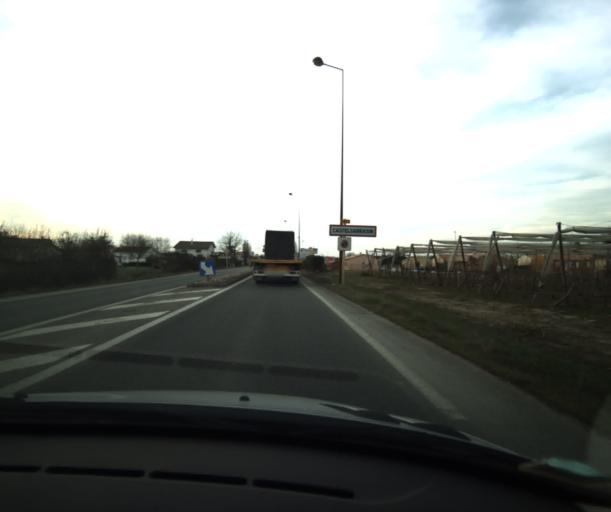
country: FR
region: Midi-Pyrenees
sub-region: Departement du Tarn-et-Garonne
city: Castelsarrasin
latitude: 44.0322
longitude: 1.1249
